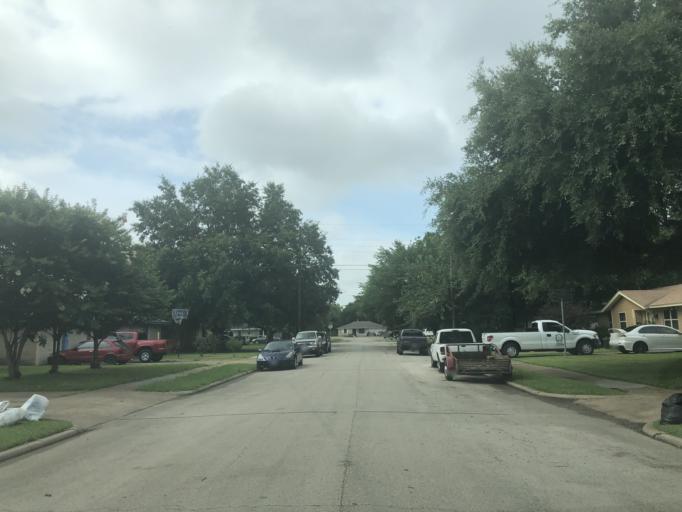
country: US
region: Texas
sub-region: Dallas County
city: Irving
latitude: 32.8058
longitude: -96.9865
